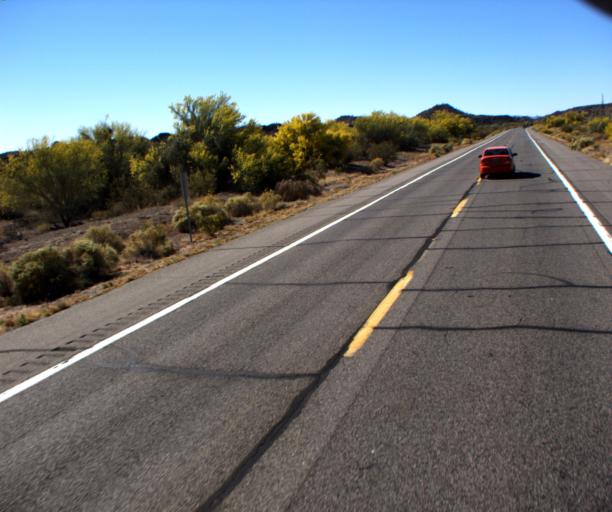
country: US
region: Arizona
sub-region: Pima County
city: Ajo
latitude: 32.5710
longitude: -112.8756
